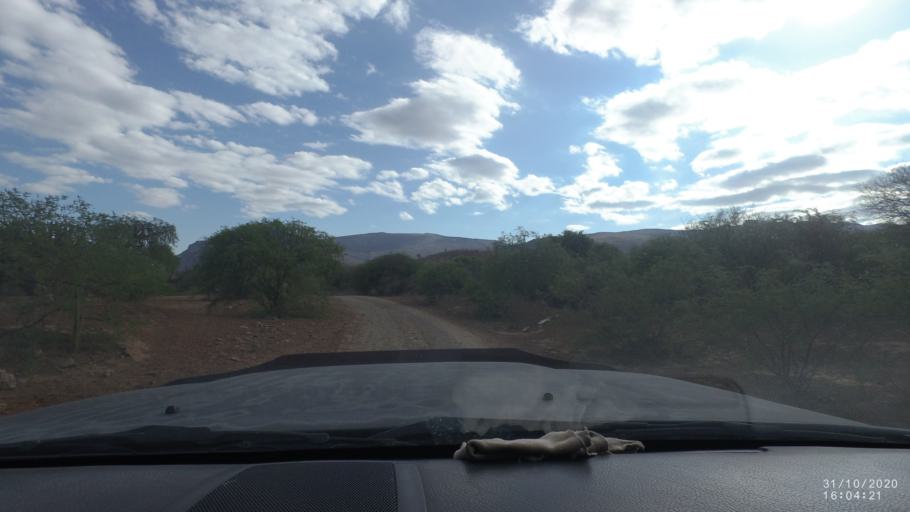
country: BO
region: Chuquisaca
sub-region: Provincia Zudanez
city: Mojocoya
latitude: -18.3589
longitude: -64.6511
